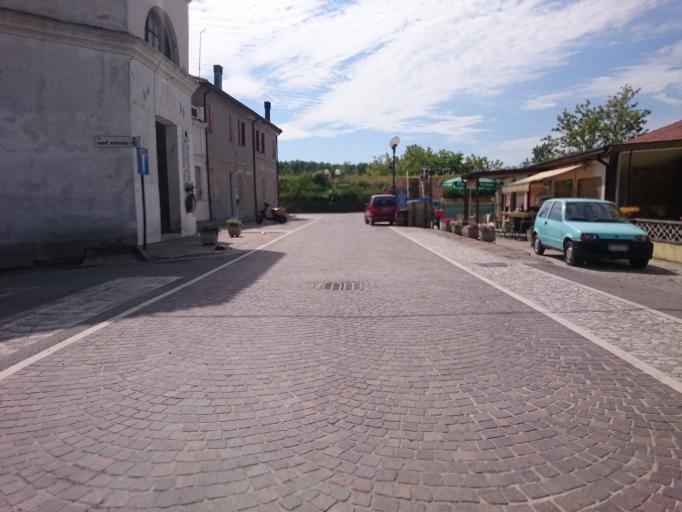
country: IT
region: Emilia-Romagna
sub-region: Provincia di Ferrara
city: Serravalle
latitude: 44.9740
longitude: 12.0727
